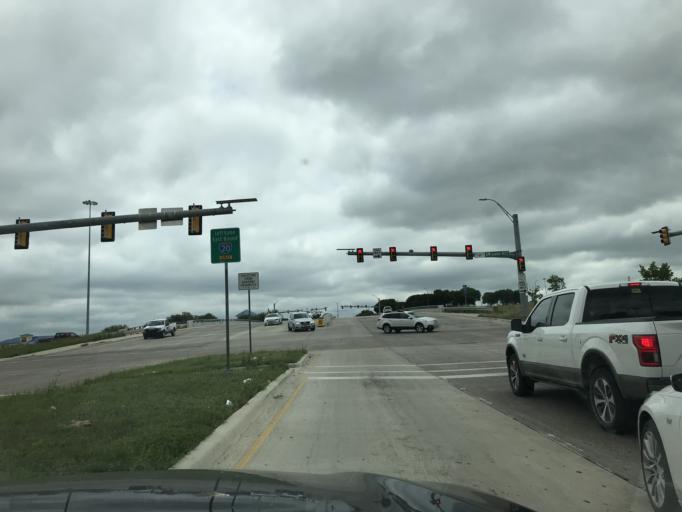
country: US
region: Texas
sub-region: Tarrant County
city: Benbrook
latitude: 32.6848
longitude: -97.4140
